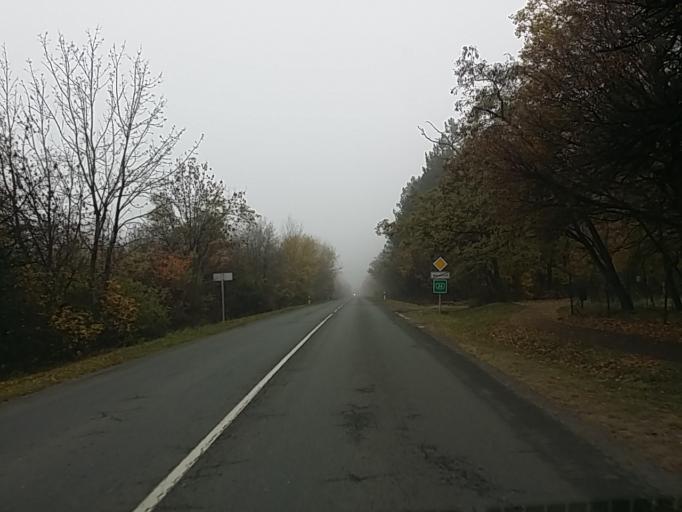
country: HU
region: Heves
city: Gyongyossolymos
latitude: 47.8228
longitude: 19.9660
